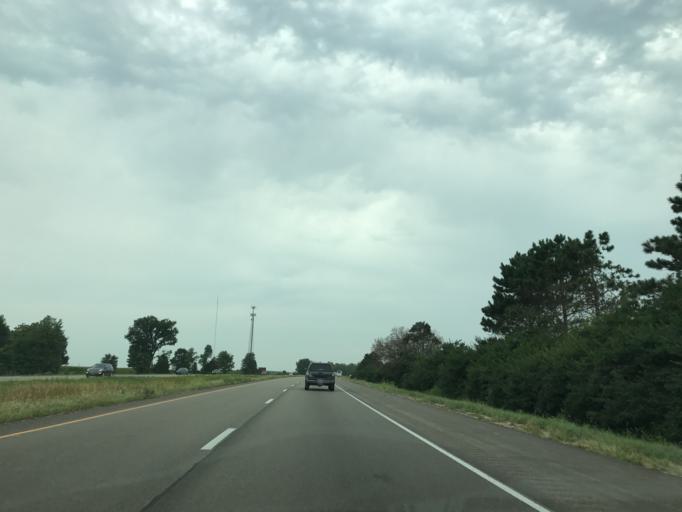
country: US
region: Illinois
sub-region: Bureau County
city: Princeton
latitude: 41.3901
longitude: -89.5149
